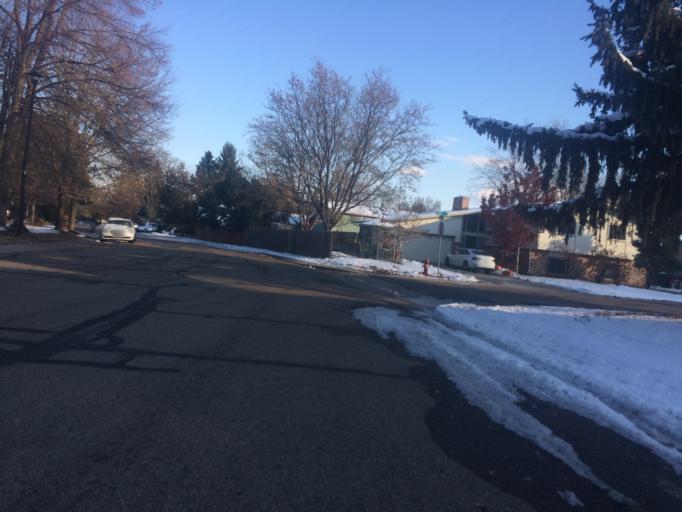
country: US
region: Colorado
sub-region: Boulder County
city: Lafayette
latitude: 39.9902
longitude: -105.1080
